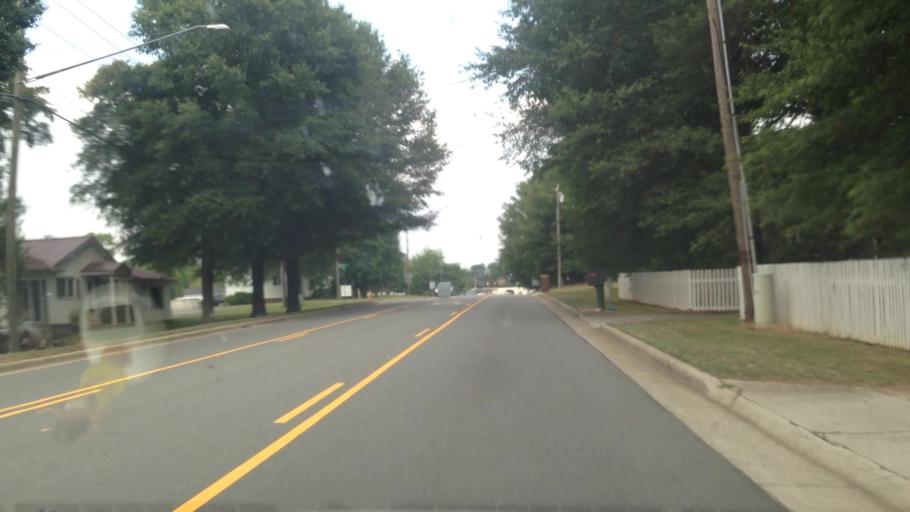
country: US
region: North Carolina
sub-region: Forsyth County
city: Walkertown
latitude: 36.1371
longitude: -80.1209
